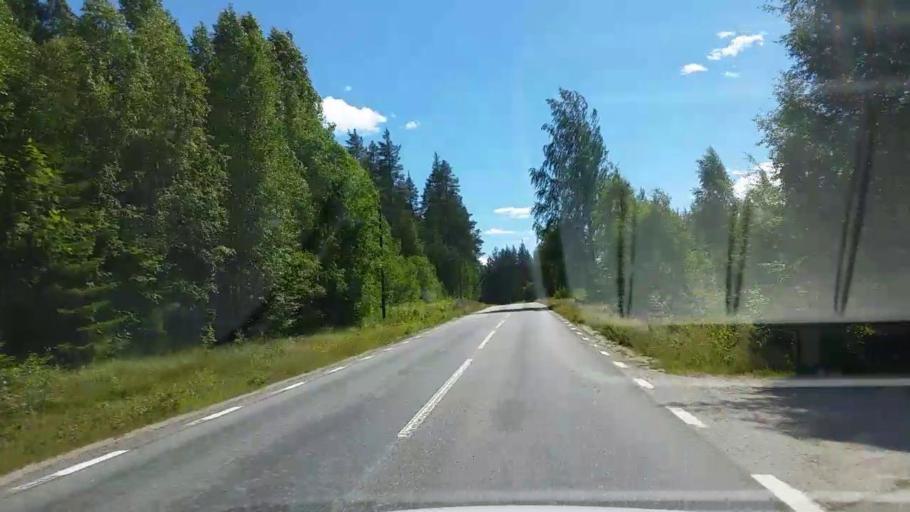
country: SE
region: Gaevleborg
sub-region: Ovanakers Kommun
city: Edsbyn
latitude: 61.2975
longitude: 15.8907
